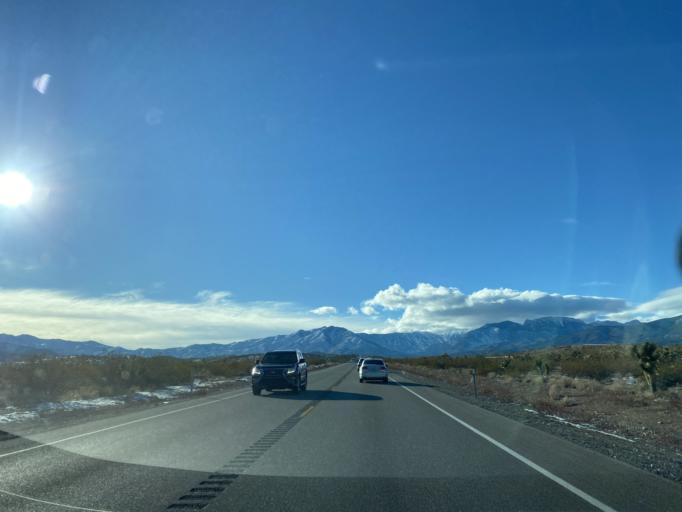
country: US
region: Nevada
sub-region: Clark County
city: Summerlin South
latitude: 36.2801
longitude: -115.4519
